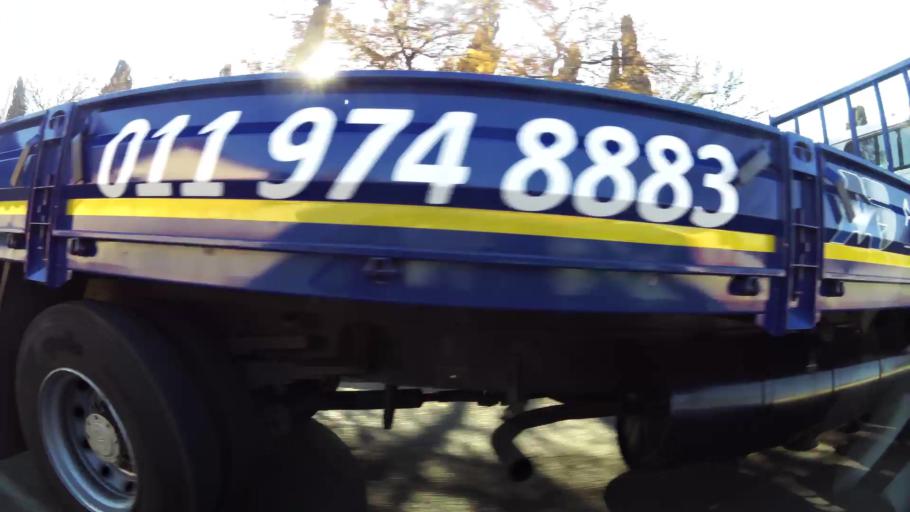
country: ZA
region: Gauteng
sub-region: City of Johannesburg Metropolitan Municipality
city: Modderfontein
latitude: -26.1459
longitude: 28.1626
